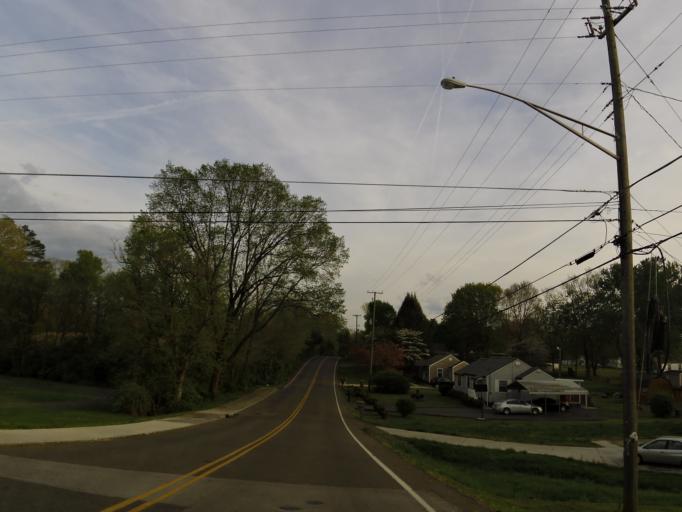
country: US
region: Tennessee
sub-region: Knox County
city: Knoxville
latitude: 36.0510
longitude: -83.9049
